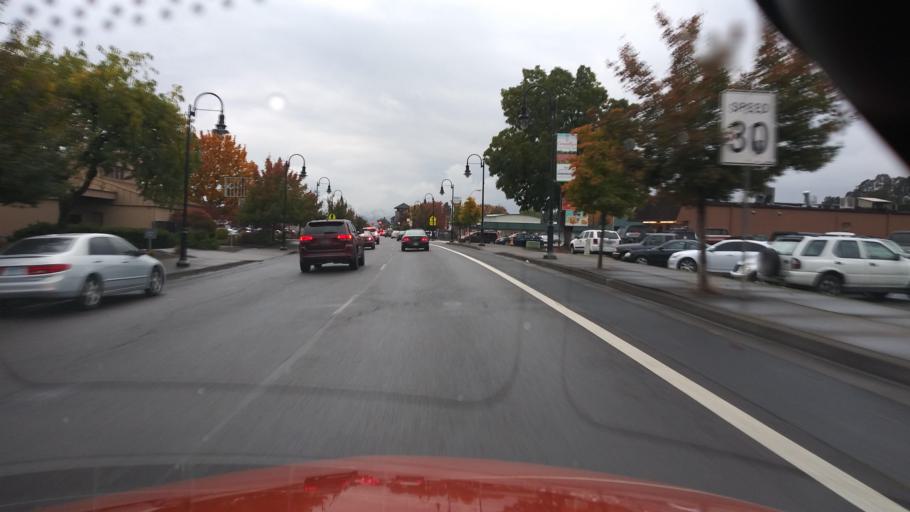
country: US
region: Oregon
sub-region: Washington County
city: Cornelius
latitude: 45.5209
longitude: -123.0503
